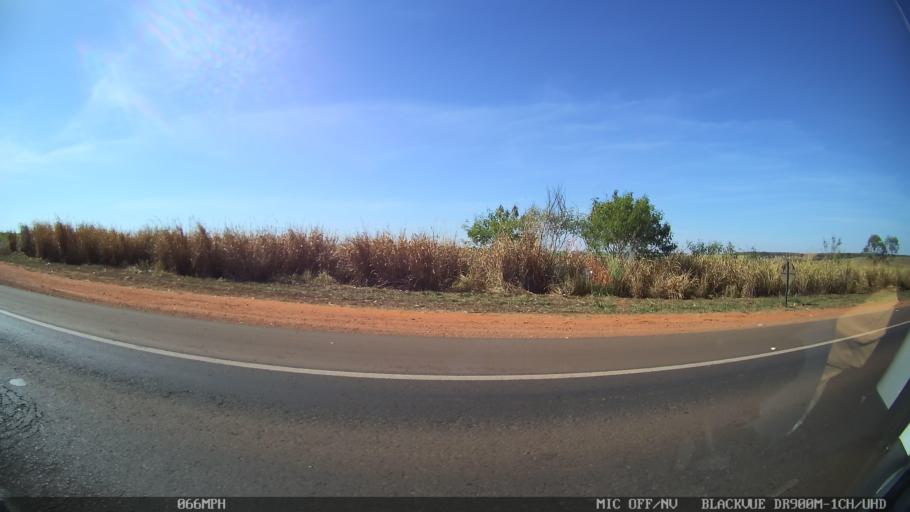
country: BR
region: Sao Paulo
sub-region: Olimpia
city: Olimpia
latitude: -20.7139
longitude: -48.8763
